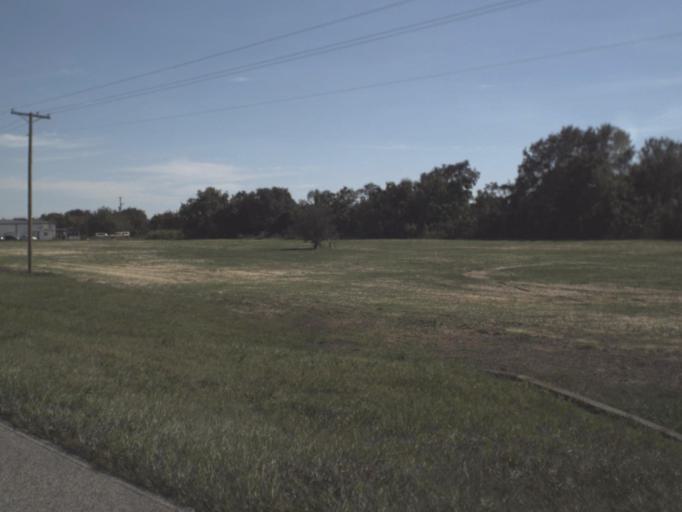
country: US
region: Florida
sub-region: Highlands County
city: Lake Placid
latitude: 27.3286
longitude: -81.3791
